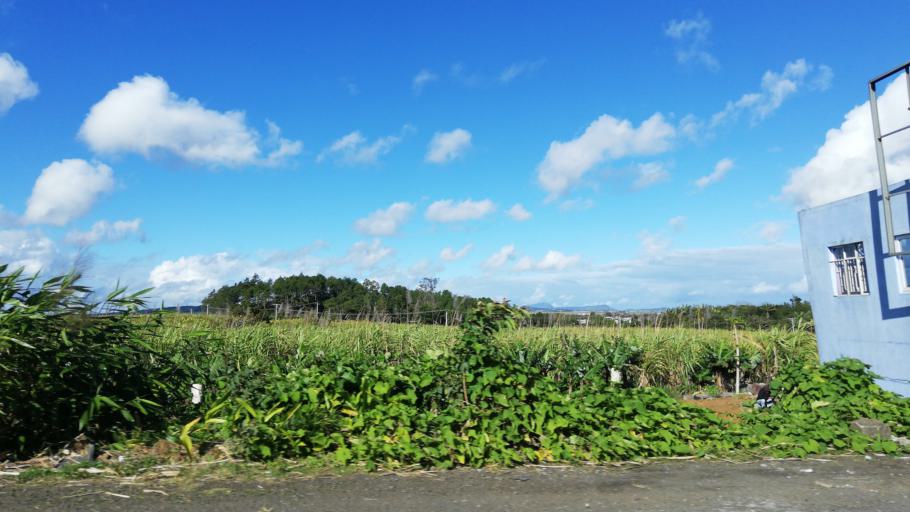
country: MU
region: Moka
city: Quartier Militaire
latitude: -20.2377
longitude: 57.5765
